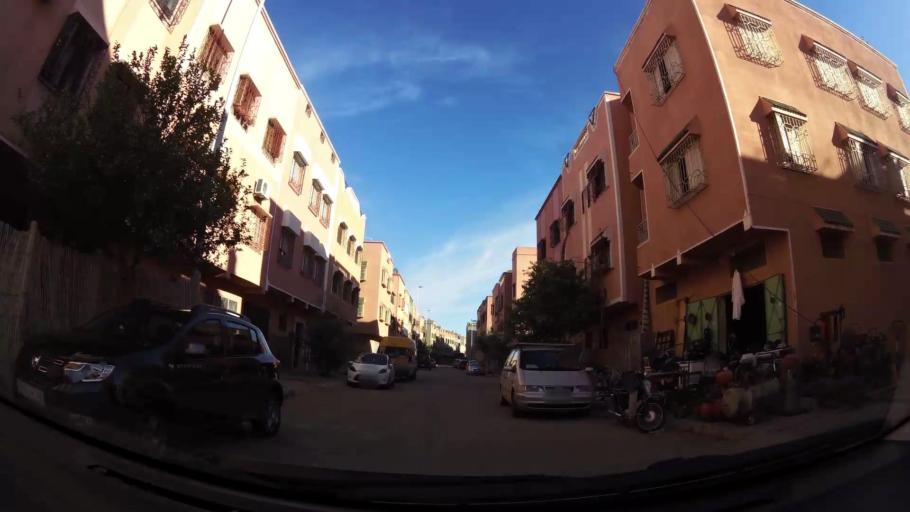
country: MA
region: Marrakech-Tensift-Al Haouz
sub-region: Marrakech
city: Marrakesh
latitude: 31.6191
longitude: -8.0702
